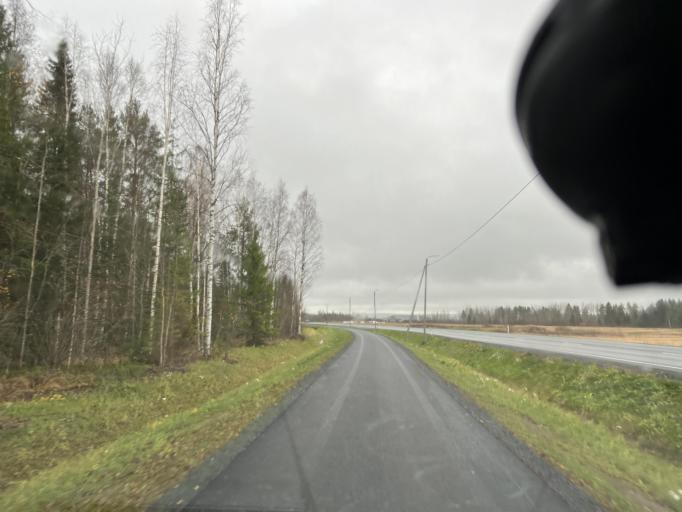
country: FI
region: Northern Ostrobothnia
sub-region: Ylivieska
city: Sievi
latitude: 63.9401
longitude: 24.5314
